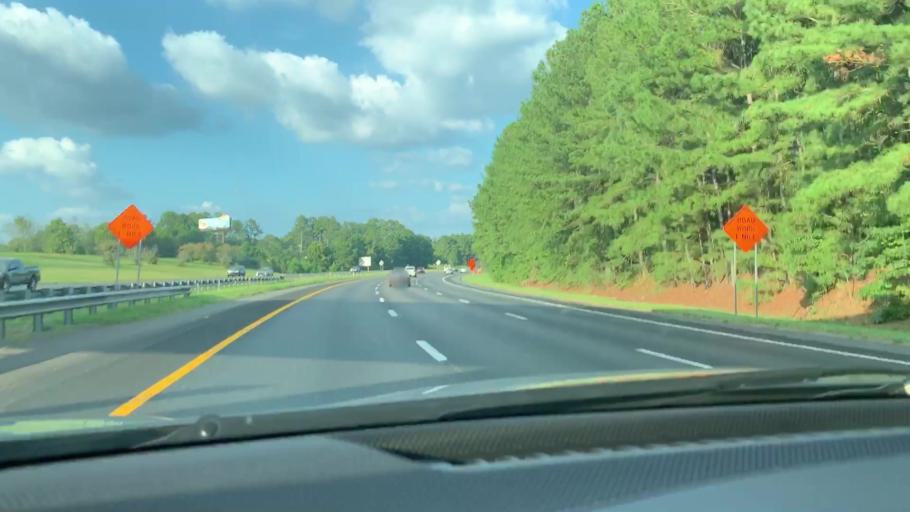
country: US
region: South Carolina
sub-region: Richland County
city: Woodfield
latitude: 34.0411
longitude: -80.9365
